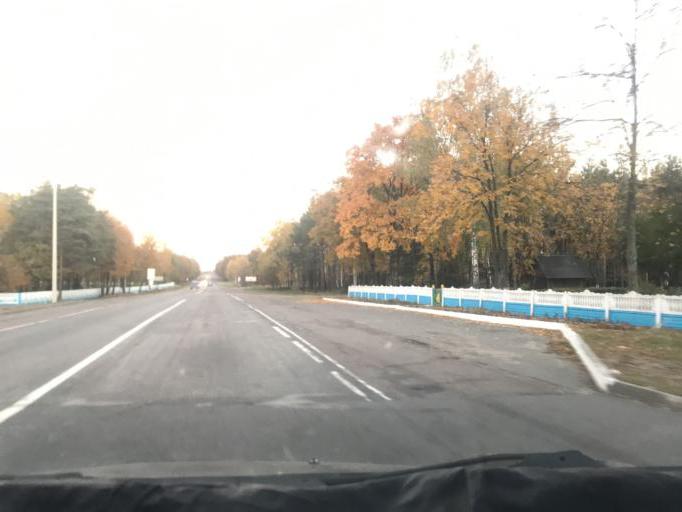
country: BY
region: Gomel
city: Kalinkavichy
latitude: 52.1260
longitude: 29.3547
